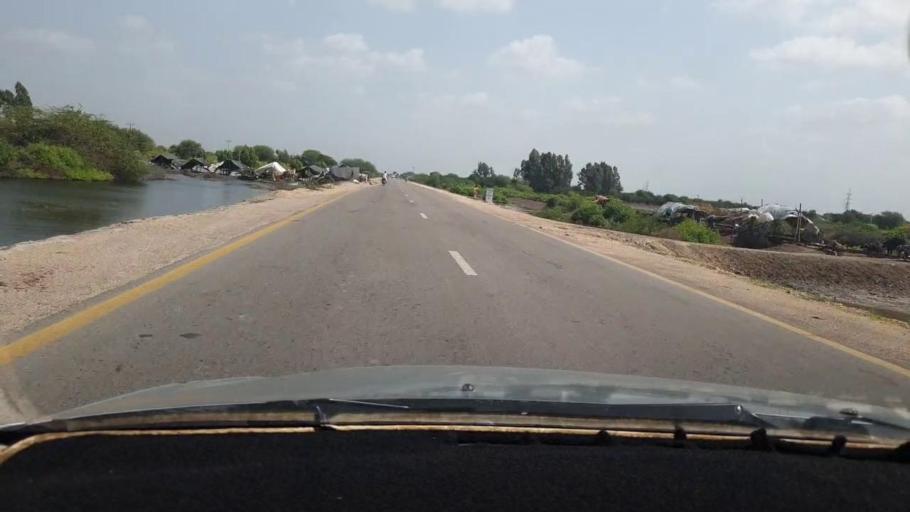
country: PK
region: Sindh
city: Digri
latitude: 25.1104
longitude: 69.1617
